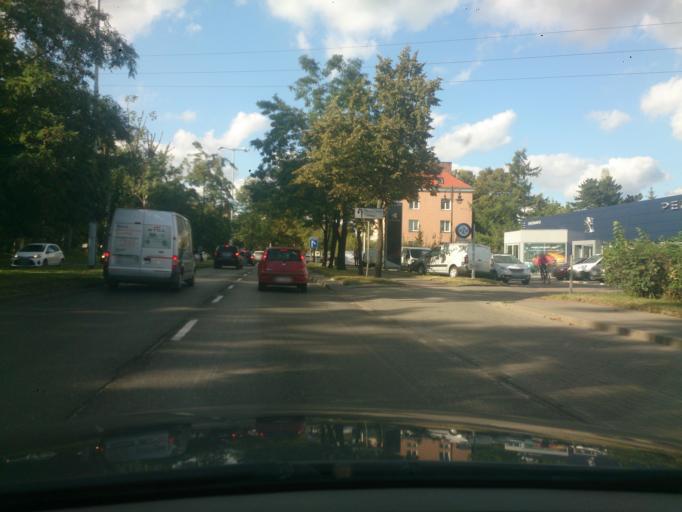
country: PL
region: Pomeranian Voivodeship
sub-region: Sopot
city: Sopot
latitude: 54.4249
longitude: 18.5636
